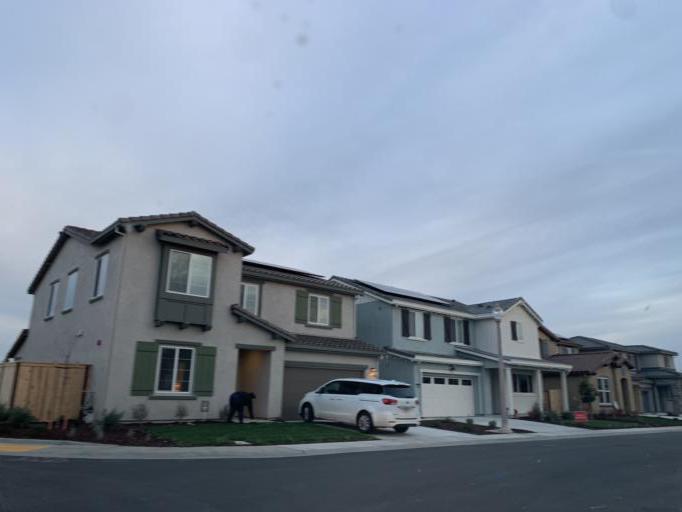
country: US
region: California
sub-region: Placer County
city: Lincoln
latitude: 38.8559
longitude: -121.2875
